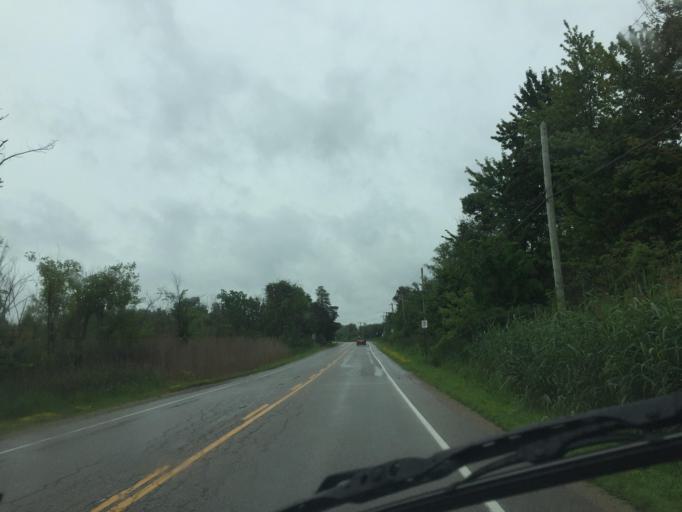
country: CA
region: Ontario
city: Cambridge
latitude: 43.4237
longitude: -80.2664
